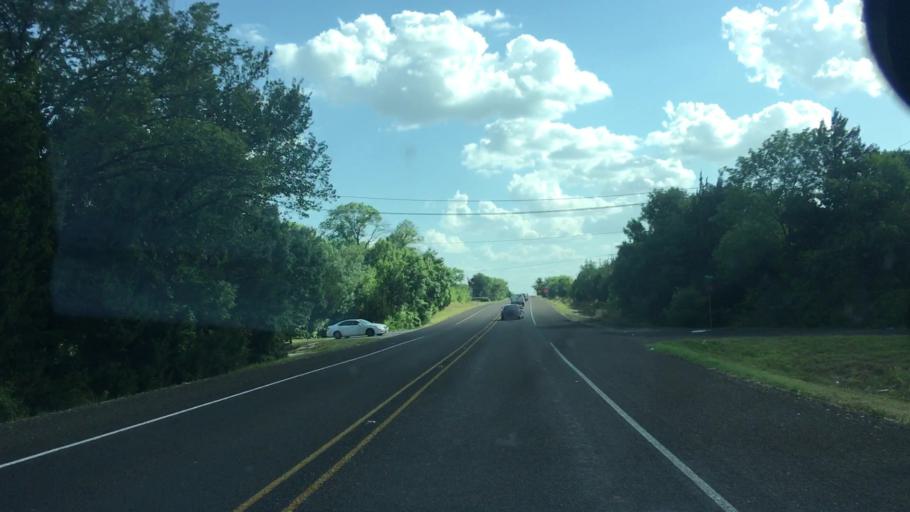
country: US
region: Texas
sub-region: Dallas County
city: Lancaster
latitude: 32.5676
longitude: -96.7632
